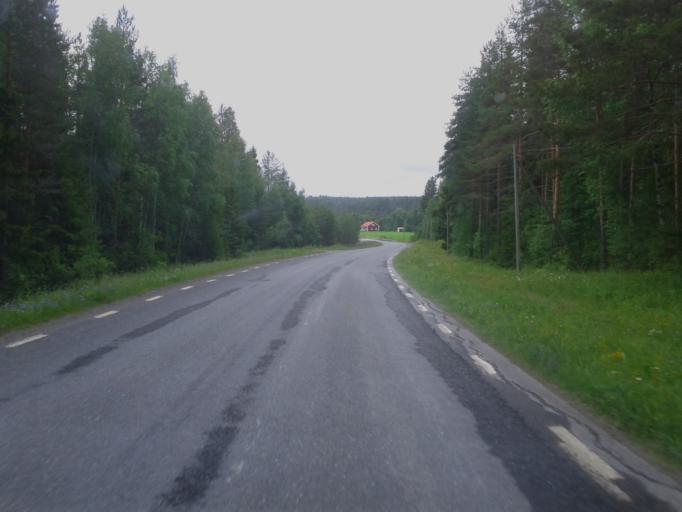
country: SE
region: Vaesterbotten
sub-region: Skelleftea Kommun
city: Forsbacka
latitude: 64.9067
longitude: 20.5975
